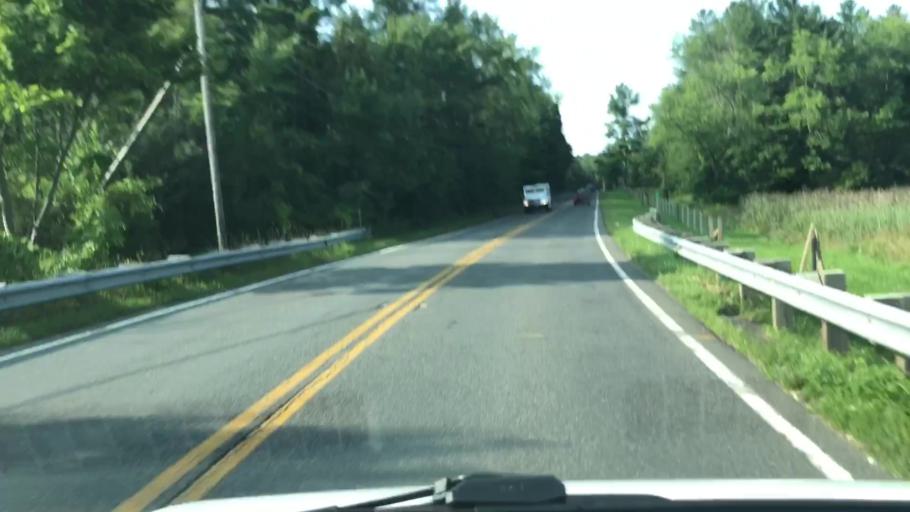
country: US
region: Massachusetts
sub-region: Berkshire County
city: Lee
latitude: 42.3137
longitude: -73.2862
